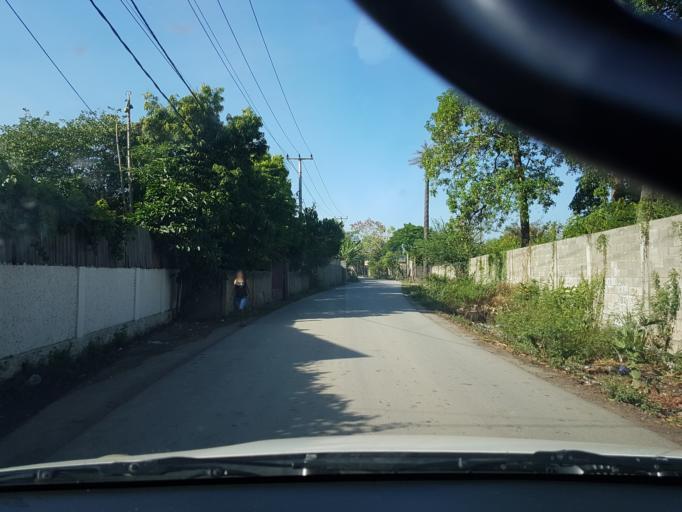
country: TL
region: Dili
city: Dili
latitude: -8.5417
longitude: 125.5424
